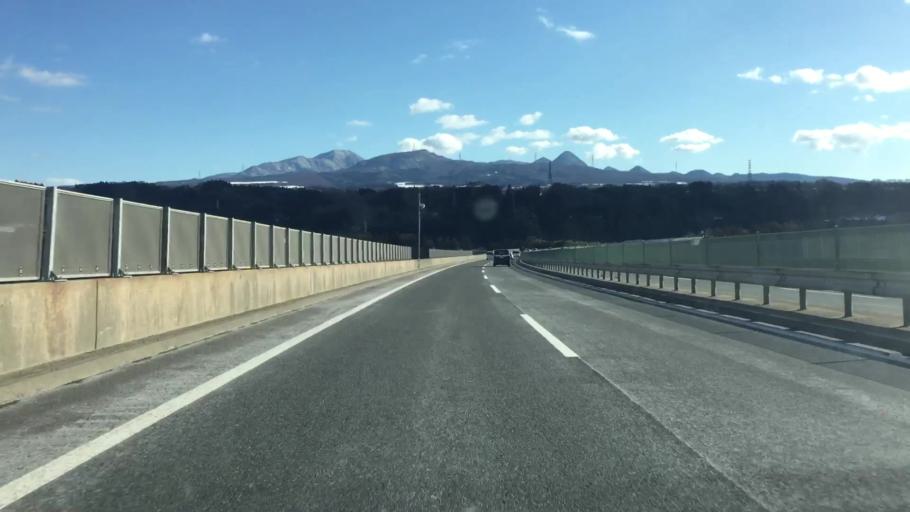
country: JP
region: Gunma
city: Numata
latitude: 36.6521
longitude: 139.0749
